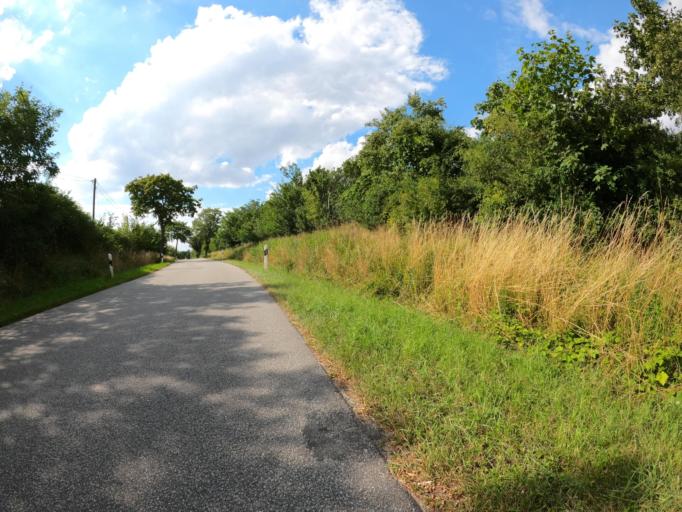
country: DE
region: Mecklenburg-Vorpommern
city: Woldegk
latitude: 53.4427
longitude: 13.5900
